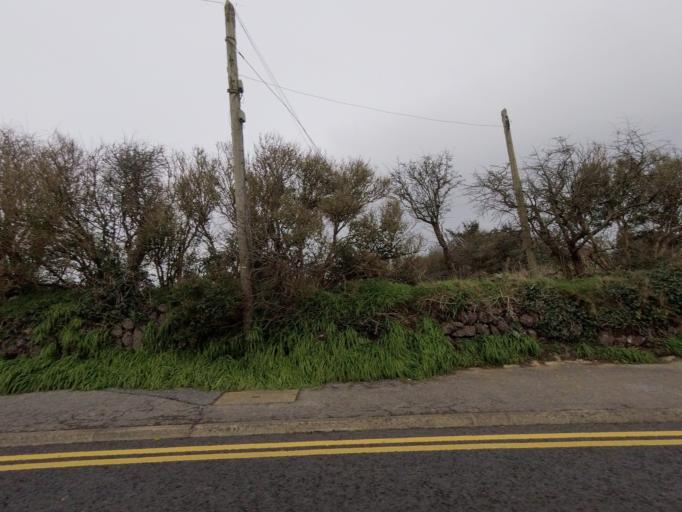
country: IE
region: Munster
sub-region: Waterford
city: Dunmore East
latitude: 52.1451
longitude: -6.9965
